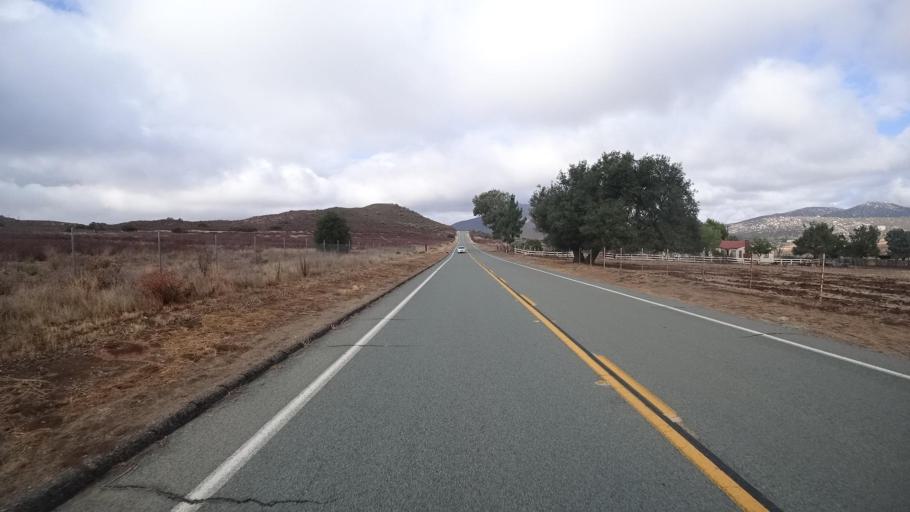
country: MX
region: Baja California
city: Tecate
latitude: 32.6151
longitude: -116.5999
